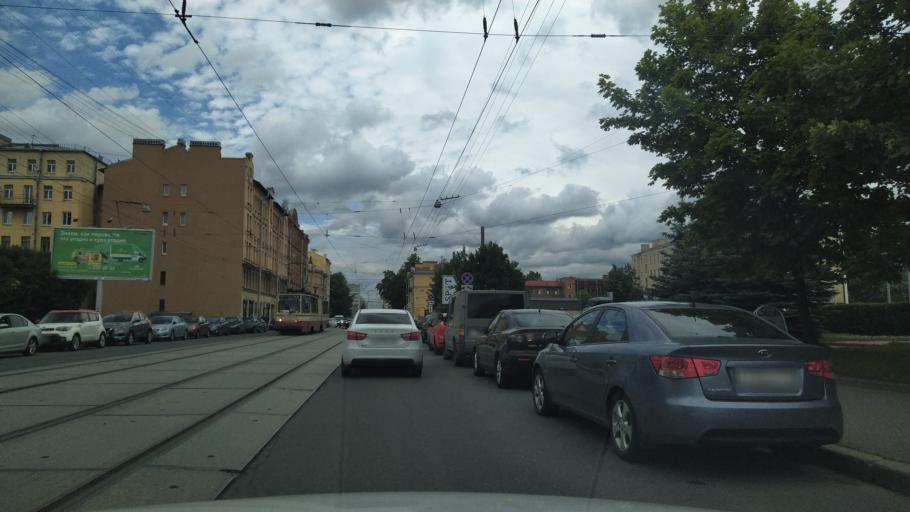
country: RU
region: Leningrad
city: Finlyandskiy
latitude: 59.9649
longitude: 30.3816
